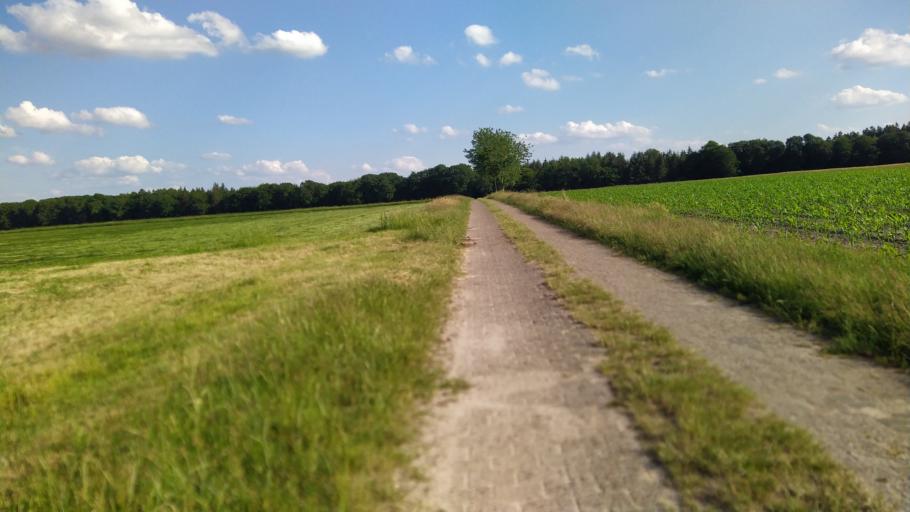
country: DE
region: Lower Saxony
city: Lintig
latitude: 53.6014
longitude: 8.8931
